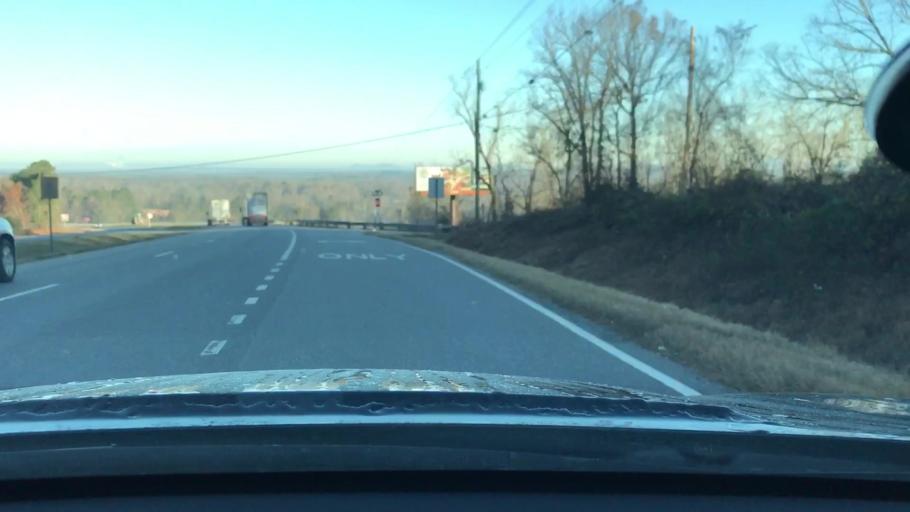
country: US
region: Alabama
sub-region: Talladega County
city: Mignon
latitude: 33.2027
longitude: -86.3074
